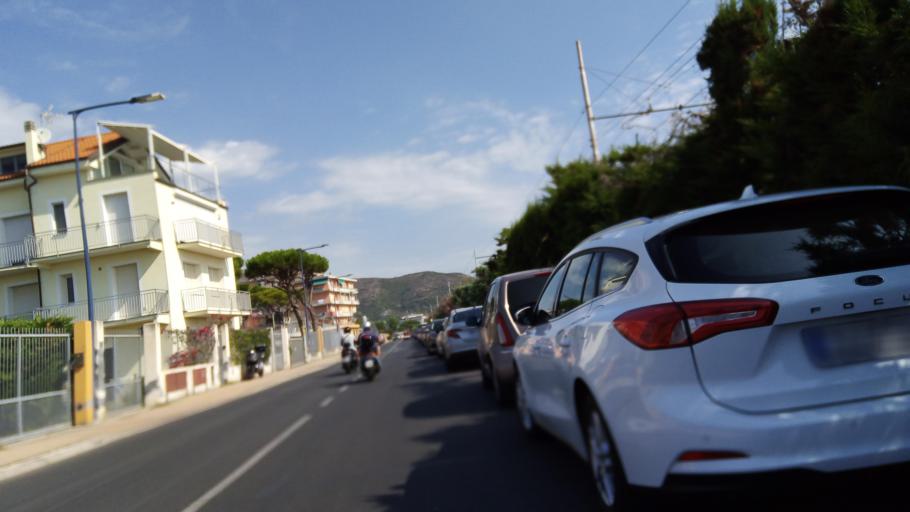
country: IT
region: Liguria
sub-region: Provincia di Savona
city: Ceriale
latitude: 44.0786
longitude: 8.2263
